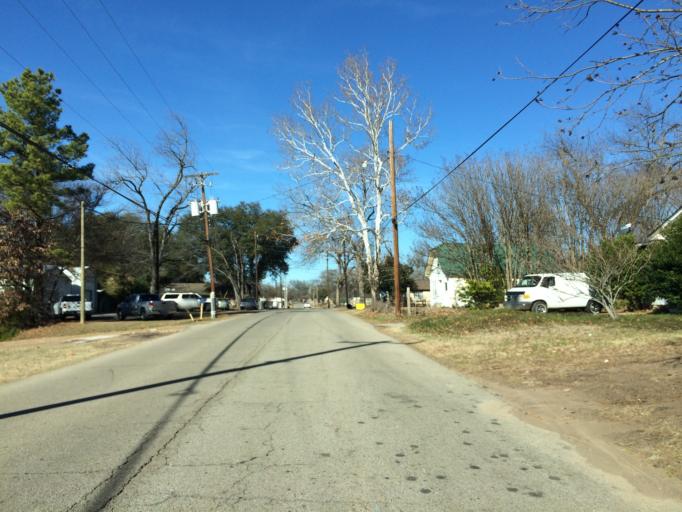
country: US
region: Texas
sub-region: Wood County
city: Mineola
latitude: 32.6735
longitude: -95.4837
